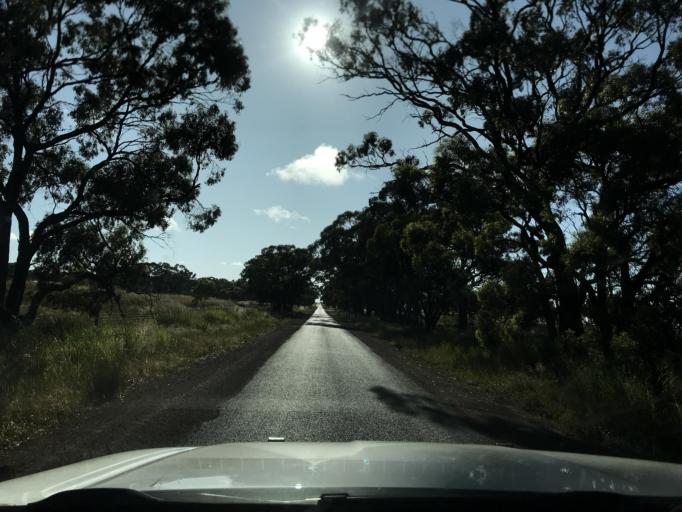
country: AU
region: Victoria
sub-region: Horsham
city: Horsham
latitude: -36.6991
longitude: 141.6155
